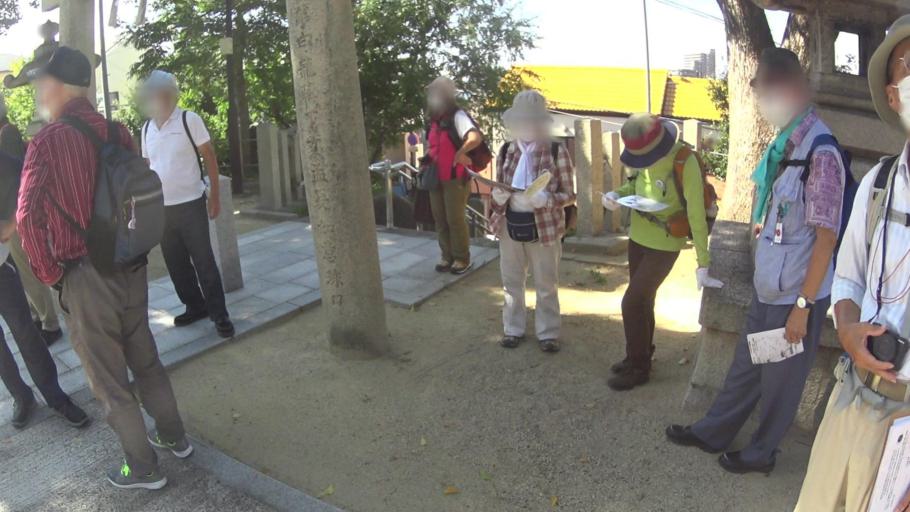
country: JP
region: Osaka
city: Izumiotsu
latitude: 34.4869
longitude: 135.4024
